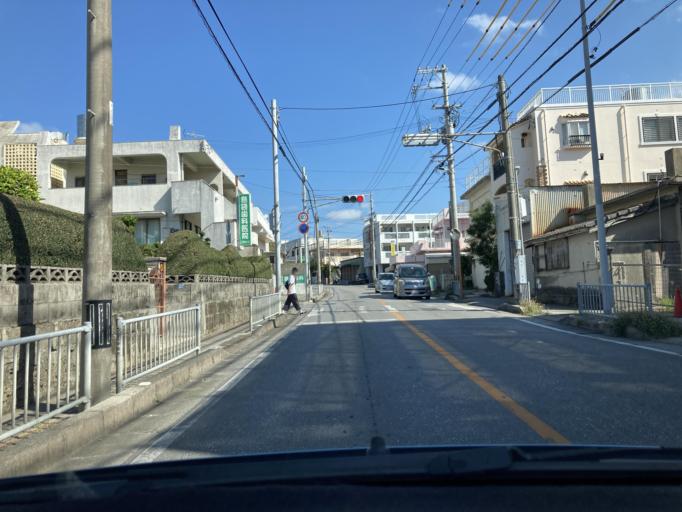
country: JP
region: Okinawa
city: Tomigusuku
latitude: 26.1832
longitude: 127.6657
